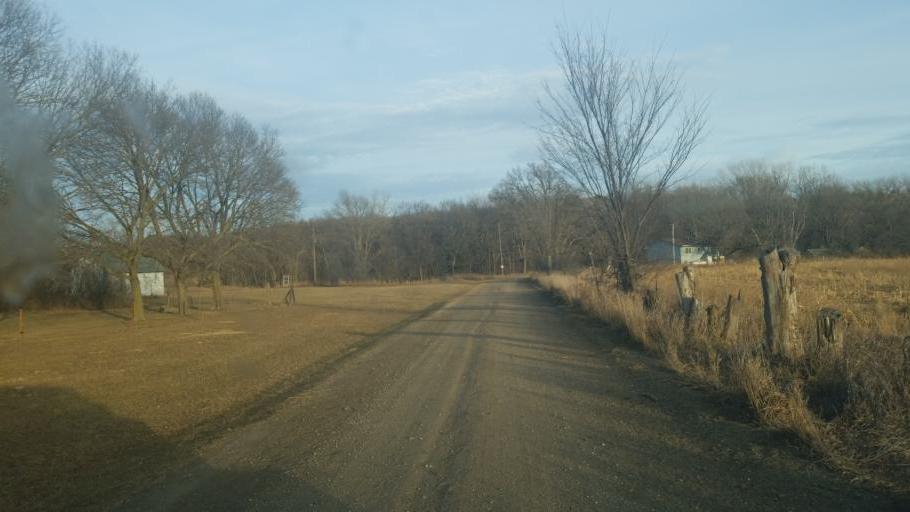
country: US
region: Nebraska
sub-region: Knox County
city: Center
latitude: 42.6802
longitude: -97.8128
